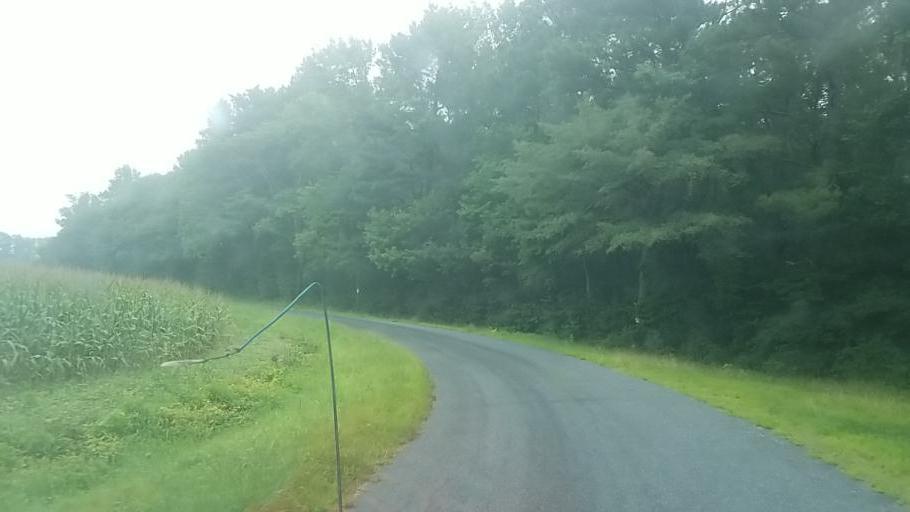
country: US
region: Delaware
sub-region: Sussex County
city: Selbyville
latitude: 38.4357
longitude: -75.2860
